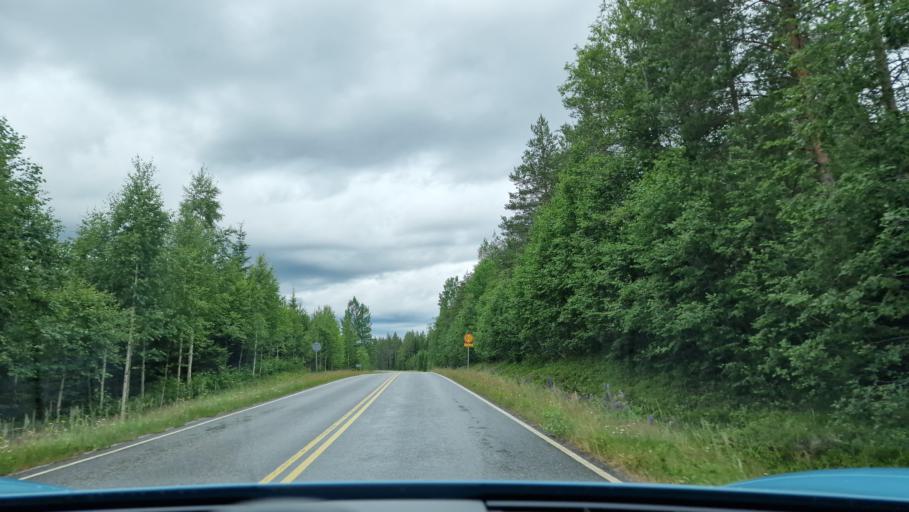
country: FI
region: Southern Ostrobothnia
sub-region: Jaerviseutu
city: Soini
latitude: 62.7035
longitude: 24.4528
